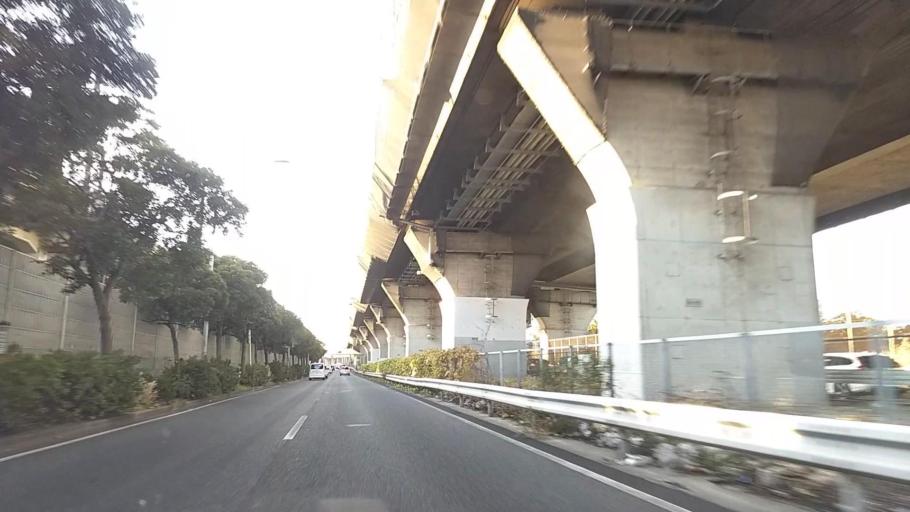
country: JP
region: Chiba
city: Funabashi
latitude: 35.6826
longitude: 139.9949
